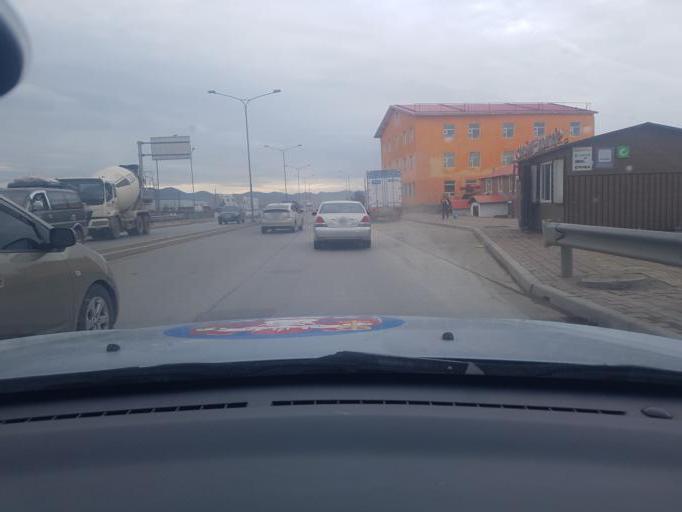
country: MN
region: Ulaanbaatar
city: Ulaanbaatar
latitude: 47.9085
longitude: 106.7855
